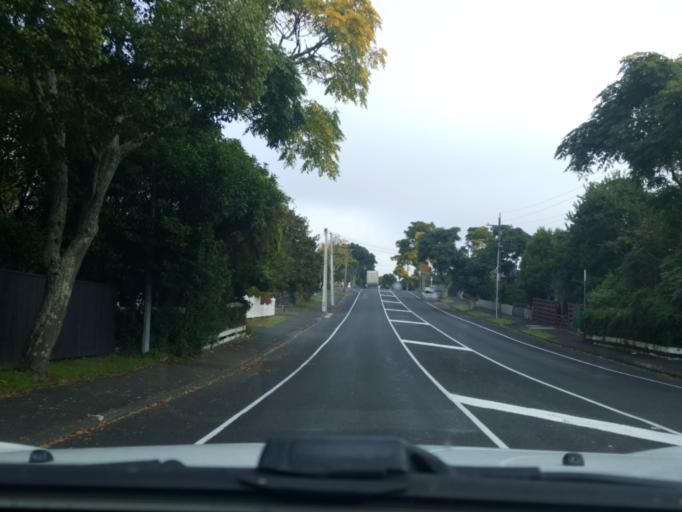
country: NZ
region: Waikato
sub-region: Hamilton City
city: Hamilton
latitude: -37.7549
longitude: 175.2878
